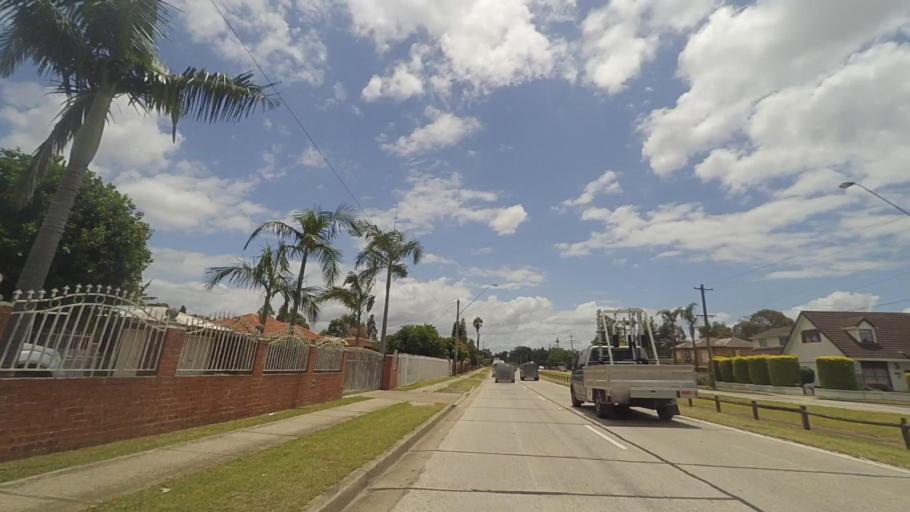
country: AU
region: New South Wales
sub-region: Fairfield
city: Fairfield Heights
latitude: -33.8792
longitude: 150.9246
